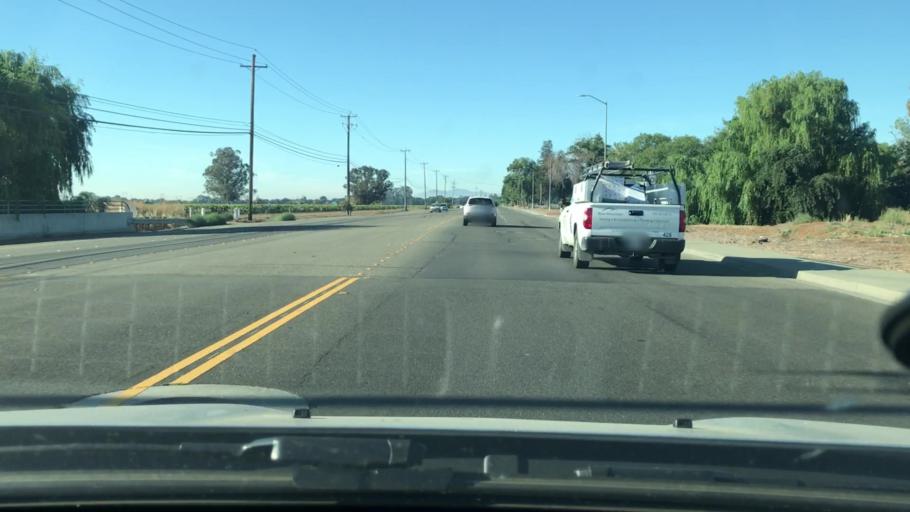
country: US
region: California
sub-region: Solano County
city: Hartley
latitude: 38.3695
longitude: -121.9340
